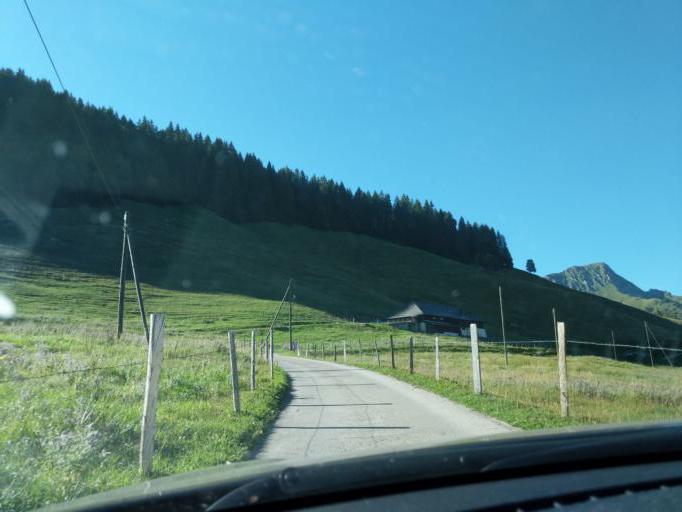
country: CH
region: Fribourg
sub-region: Gruyere District
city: Charmey
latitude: 46.5950
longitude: 7.2673
